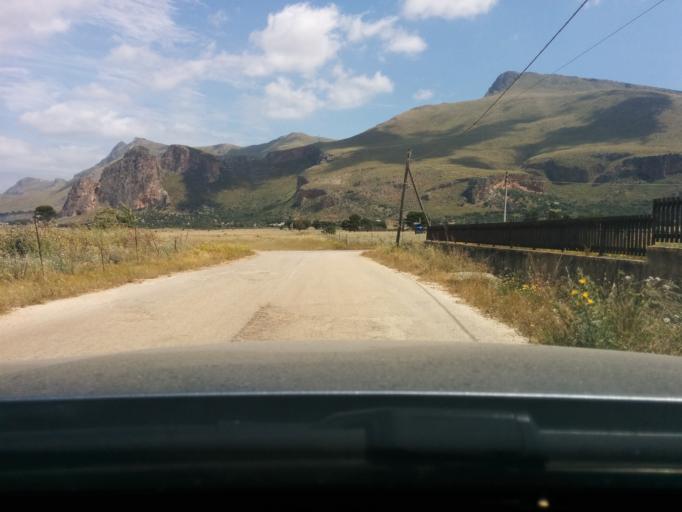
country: IT
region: Sicily
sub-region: Trapani
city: Castelluzzo
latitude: 38.1102
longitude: 12.7240
